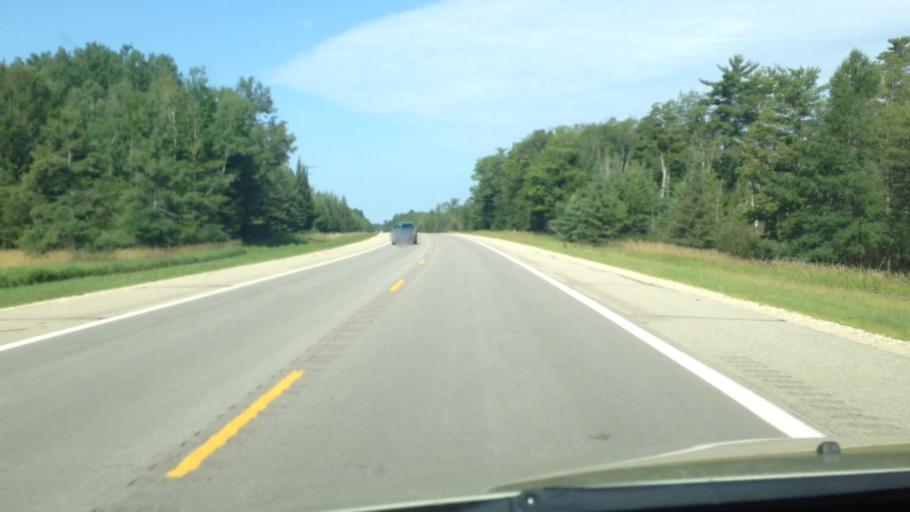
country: US
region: Michigan
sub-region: Schoolcraft County
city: Manistique
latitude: 45.9108
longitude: -86.4553
